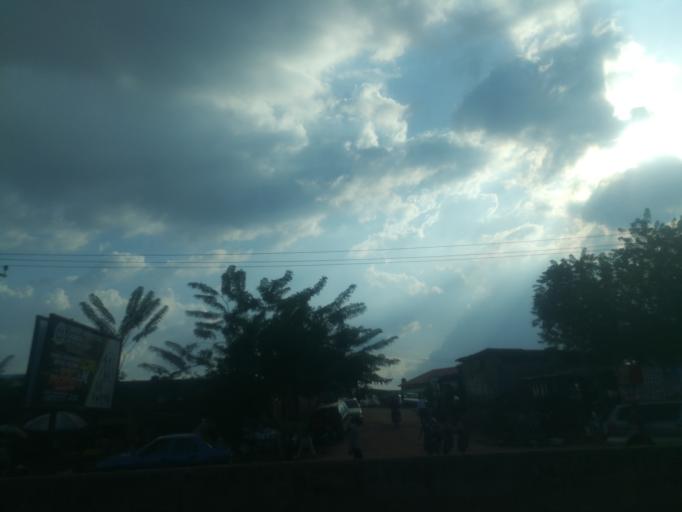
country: NG
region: Oyo
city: Ibadan
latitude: 7.3990
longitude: 3.9505
